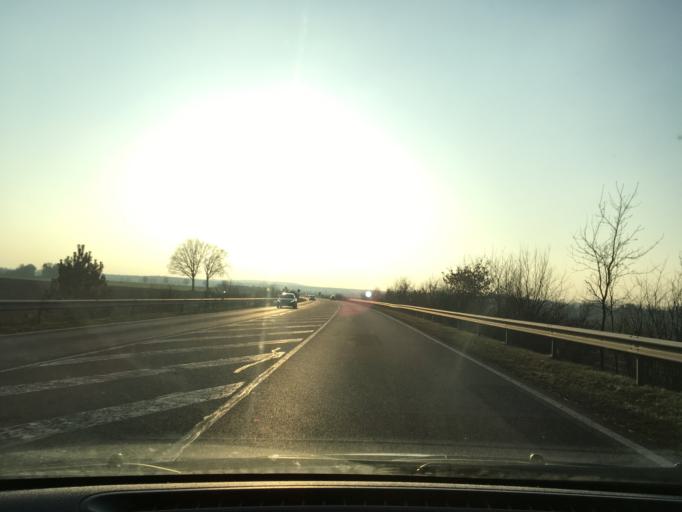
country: DE
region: Lower Saxony
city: Wrestedt
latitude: 52.9289
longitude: 10.5451
